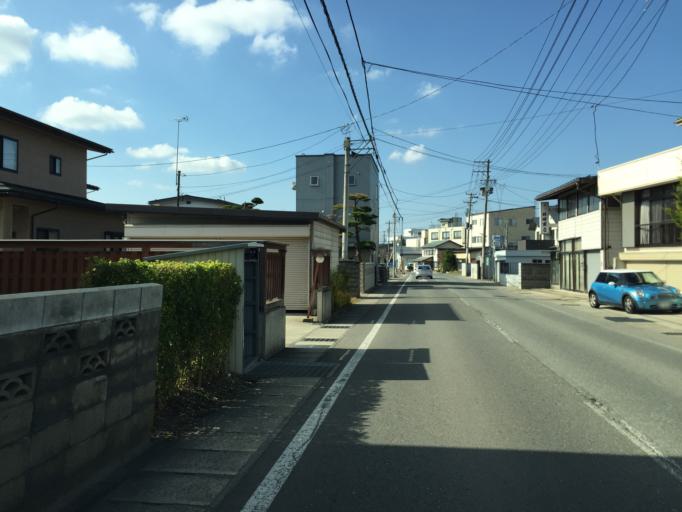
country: JP
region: Yamagata
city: Yonezawa
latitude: 37.9082
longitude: 140.1233
